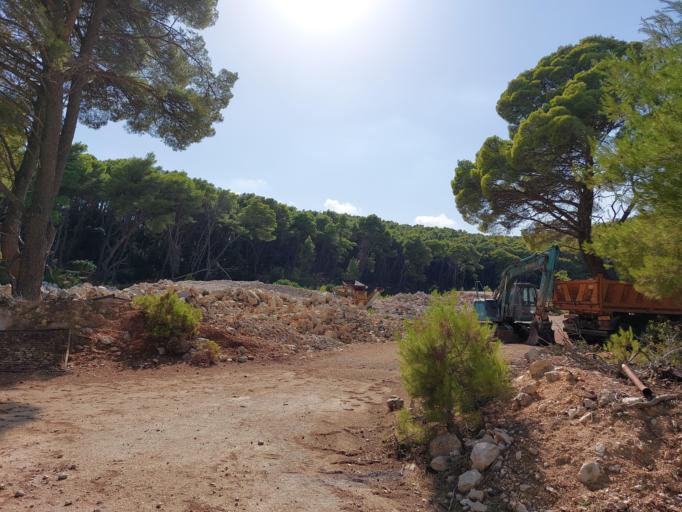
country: HR
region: Dubrovacko-Neretvanska
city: Smokvica
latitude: 42.7371
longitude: 16.8278
